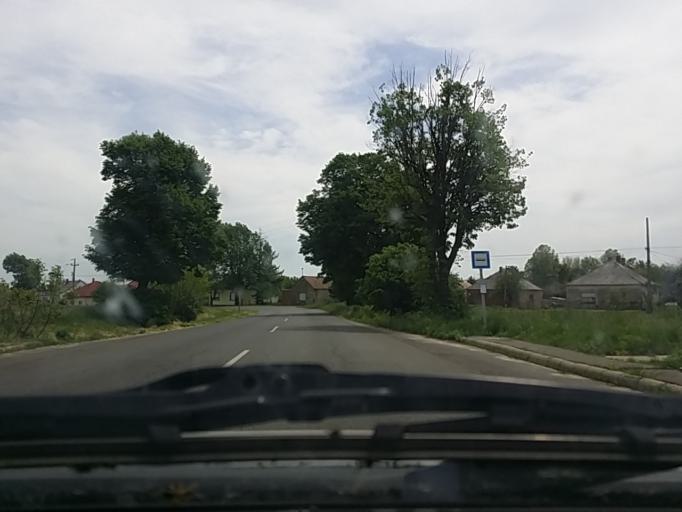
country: HU
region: Somogy
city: Barcs
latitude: 45.9664
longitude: 17.4482
